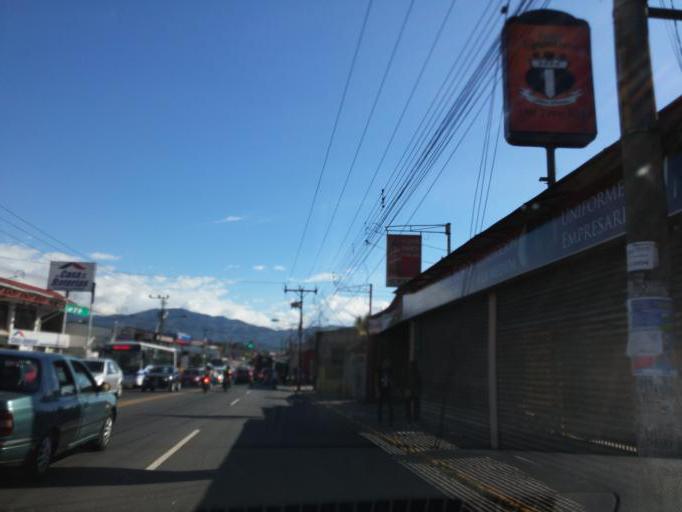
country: CR
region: San Jose
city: San Pedro
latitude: 9.9120
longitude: -84.0689
